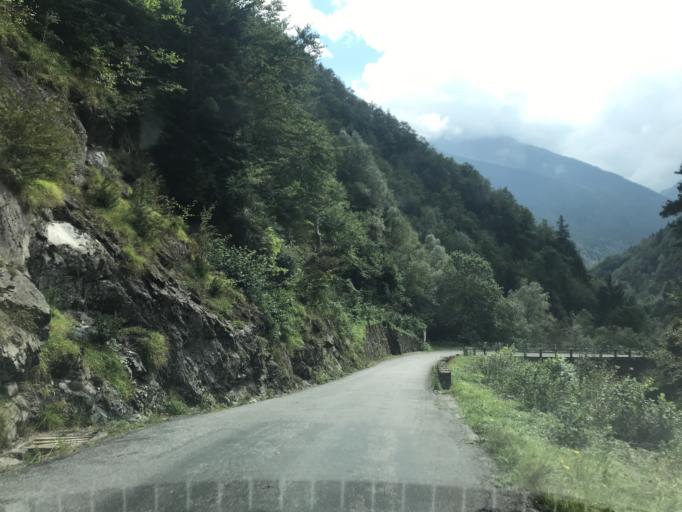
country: FR
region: Midi-Pyrenees
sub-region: Departement des Hautes-Pyrenees
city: Saint-Lary-Soulan
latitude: 42.7996
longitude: 0.2300
